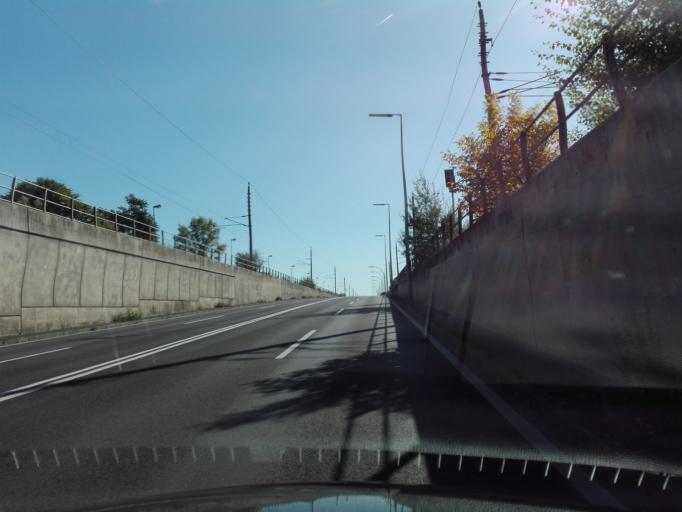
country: AT
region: Upper Austria
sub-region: Linz Stadt
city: Linz
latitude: 48.2716
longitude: 14.3201
